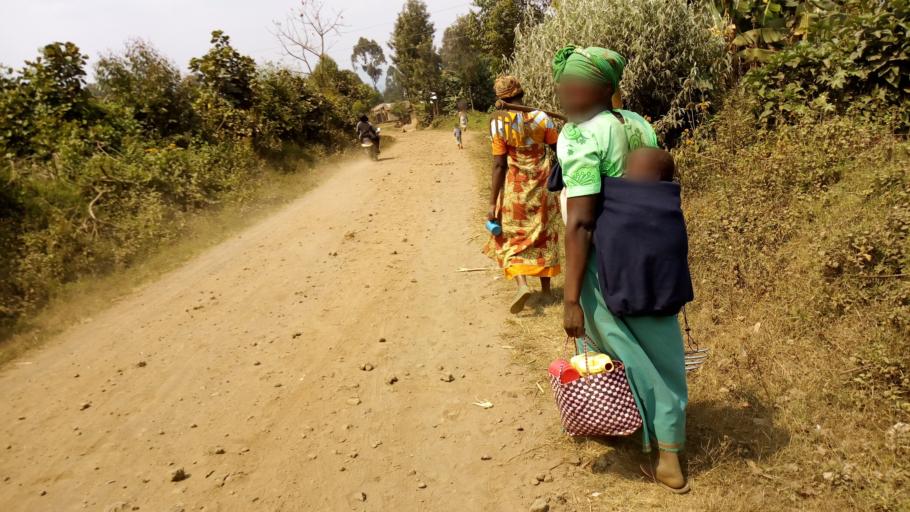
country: UG
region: Western Region
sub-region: Kisoro District
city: Kisoro
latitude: -1.3151
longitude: 29.7206
